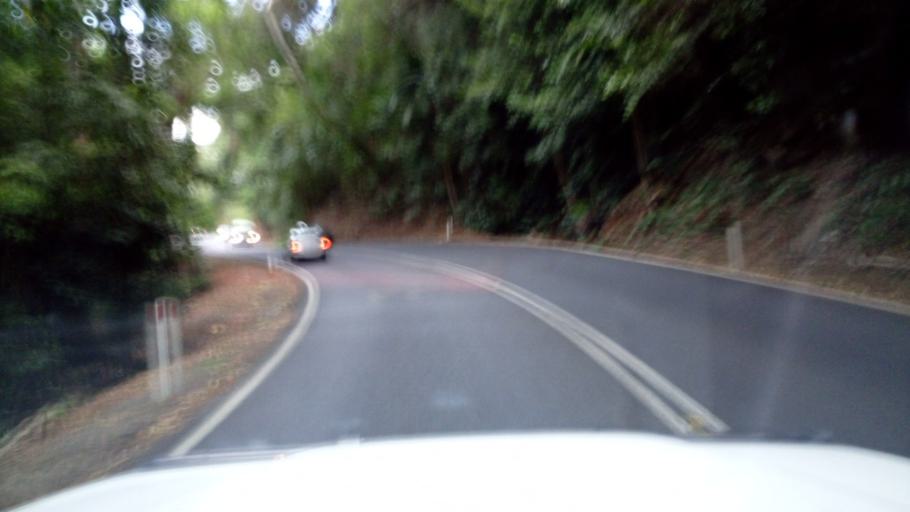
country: AU
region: Queensland
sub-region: Cairns
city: Redlynch
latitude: -16.8477
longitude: 145.6778
